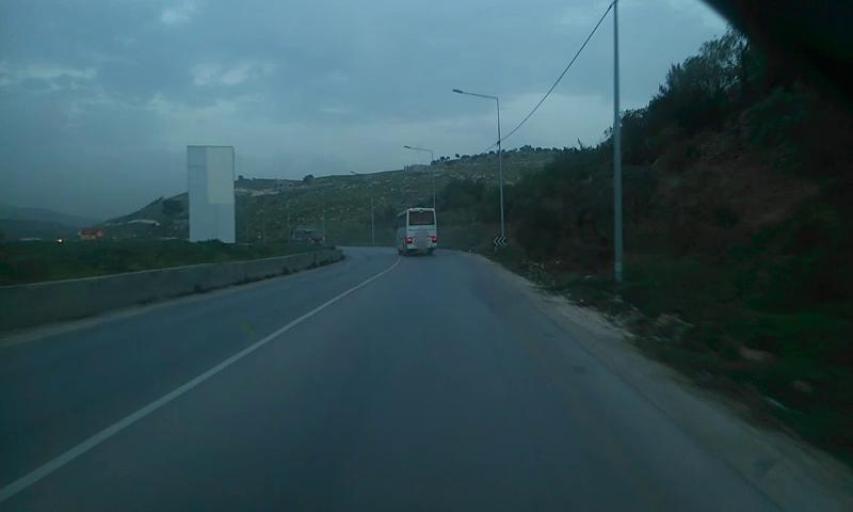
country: PS
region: West Bank
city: Iktabah
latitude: 32.3181
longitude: 35.0673
